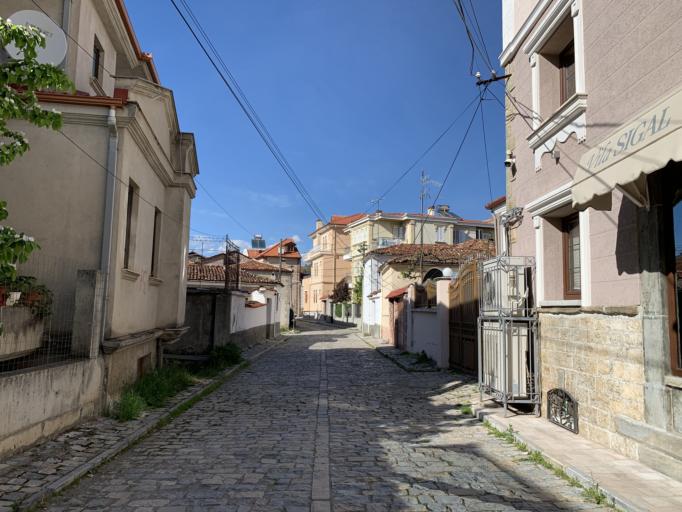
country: AL
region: Korce
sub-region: Rrethi i Korces
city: Korce
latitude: 40.6185
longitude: 20.7846
